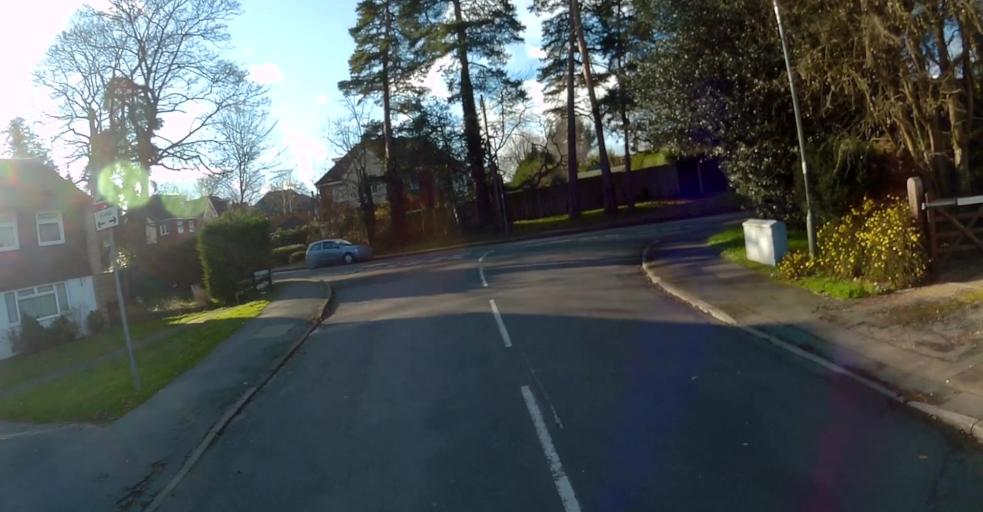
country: GB
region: England
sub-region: Surrey
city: Addlestone
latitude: 51.3643
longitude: -0.5062
